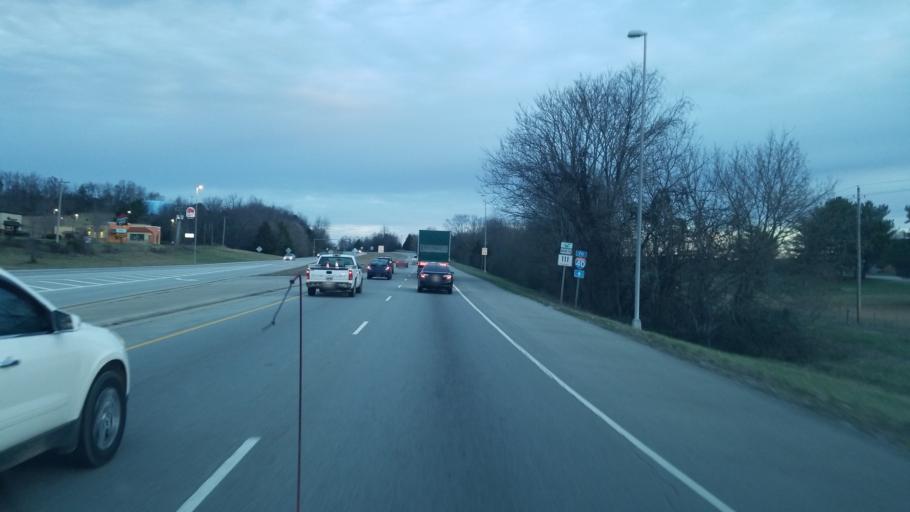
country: US
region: Tennessee
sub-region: White County
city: Sparta
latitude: 35.9442
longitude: -85.4838
